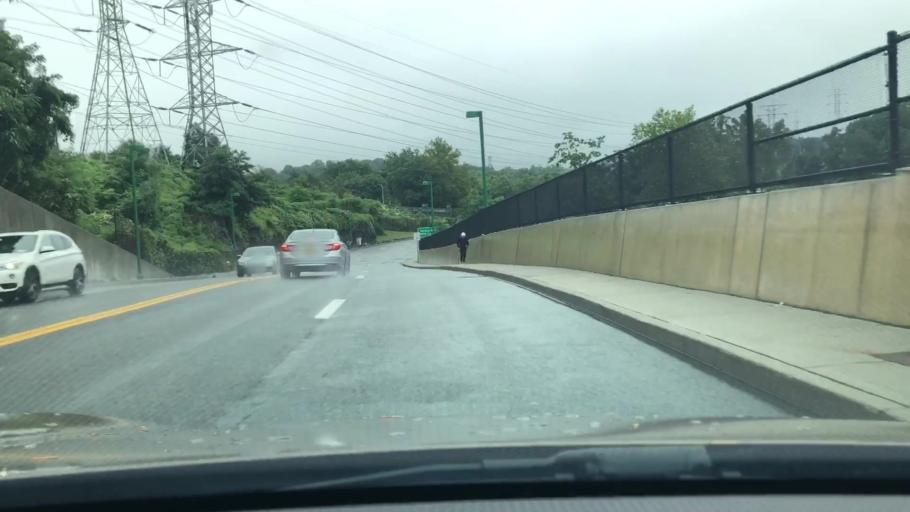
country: US
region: New York
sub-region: Westchester County
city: Tuckahoe
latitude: 40.9554
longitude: -73.8568
